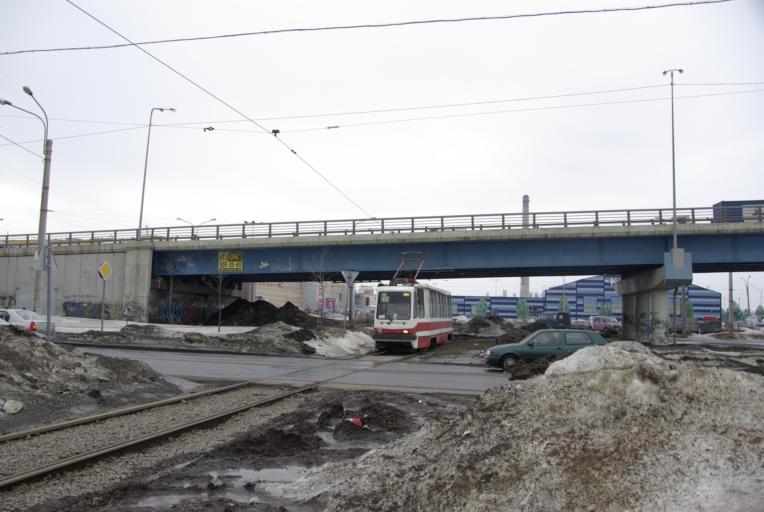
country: RU
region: Leningrad
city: Parnas
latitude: 60.0598
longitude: 30.3414
